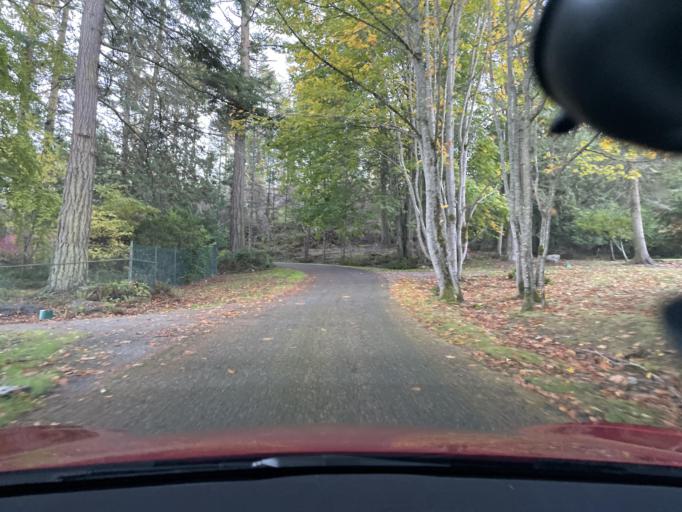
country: US
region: Washington
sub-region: San Juan County
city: Friday Harbor
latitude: 48.6192
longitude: -123.1431
